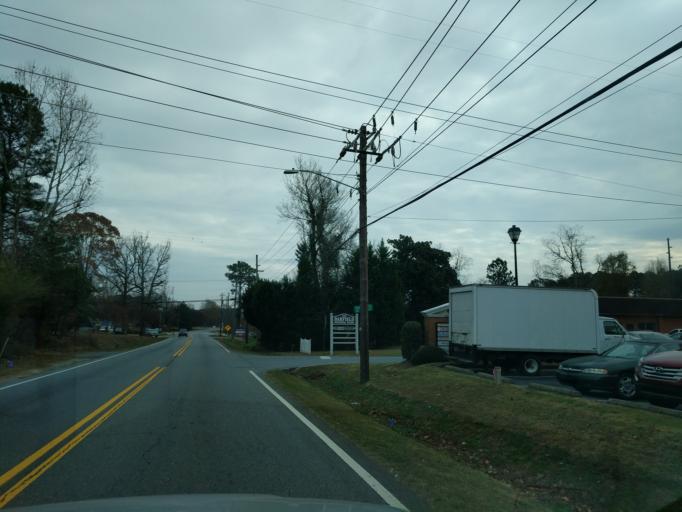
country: US
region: Georgia
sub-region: Gwinnett County
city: Duluth
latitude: 33.9982
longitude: -84.1391
